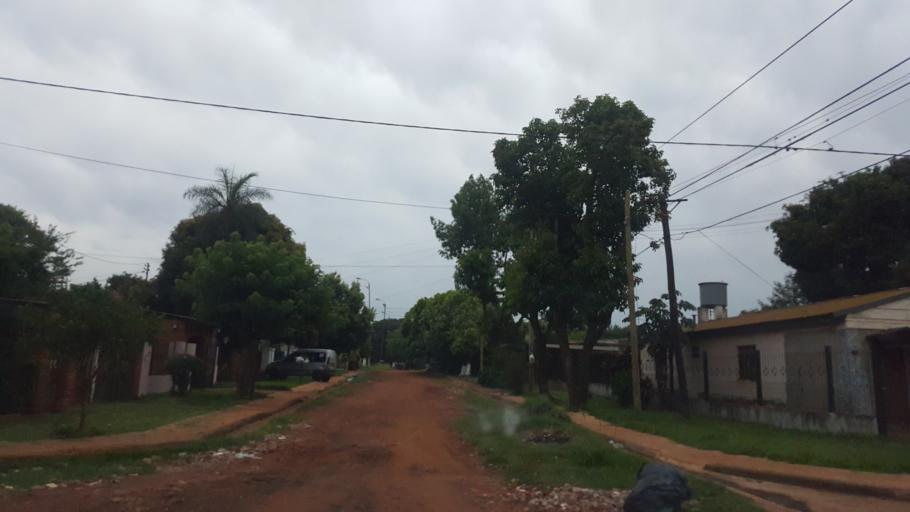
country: AR
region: Misiones
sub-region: Departamento de Capital
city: Posadas
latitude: -27.3687
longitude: -55.9270
